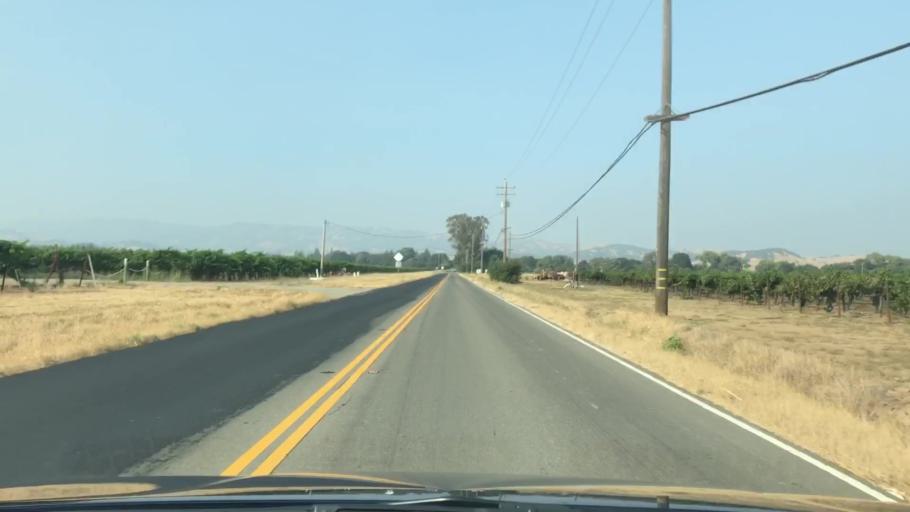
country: US
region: California
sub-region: Solano County
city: Green Valley
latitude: 38.2556
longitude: -122.1203
